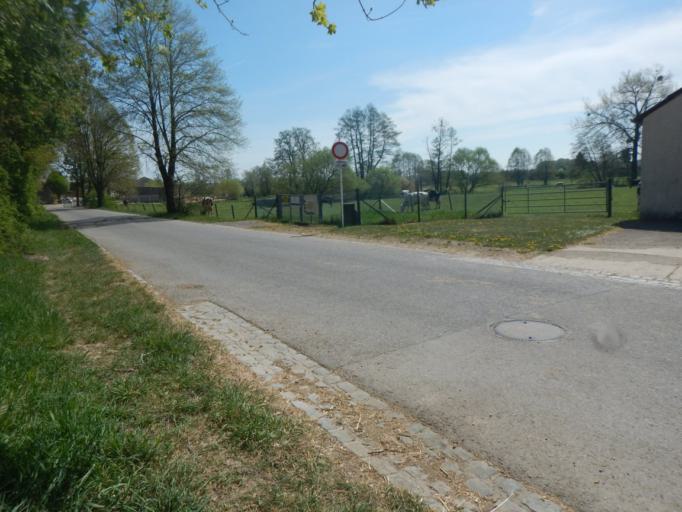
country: LU
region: Diekirch
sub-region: Canton de Redange
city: Redange-sur-Attert
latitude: 49.7549
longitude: 5.9133
